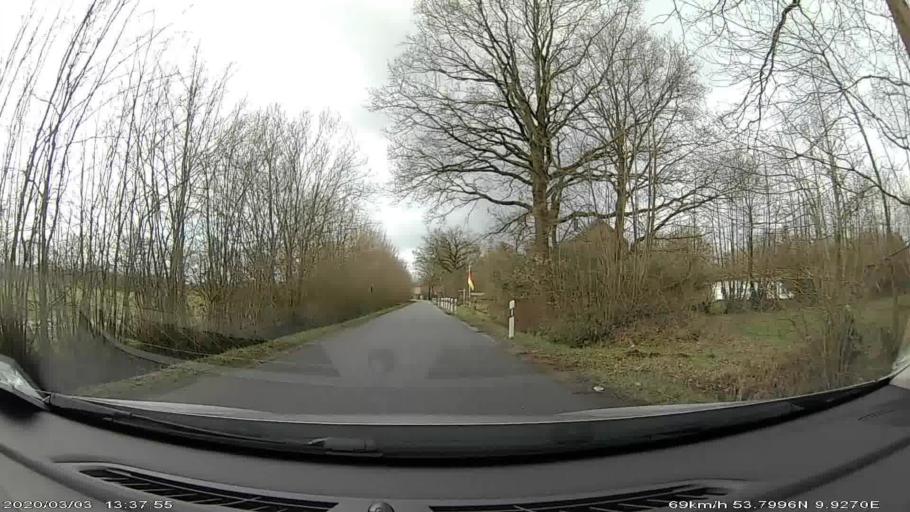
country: DE
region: Schleswig-Holstein
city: Alveslohe
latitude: 53.8000
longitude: 9.9252
